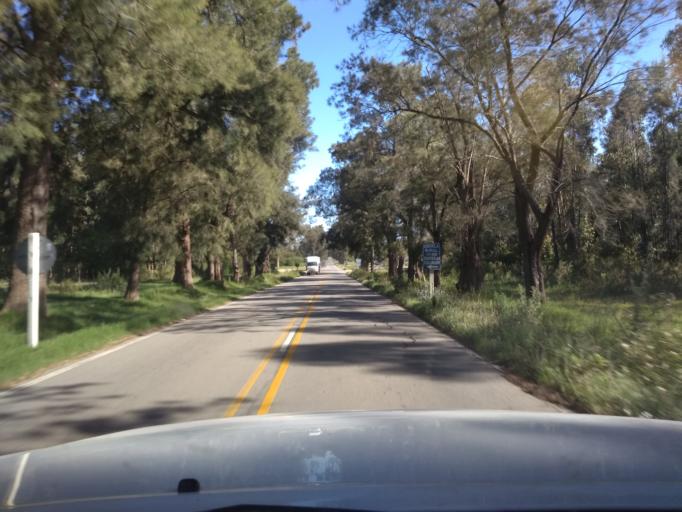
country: UY
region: Canelones
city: San Bautista
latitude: -34.3812
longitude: -55.9595
